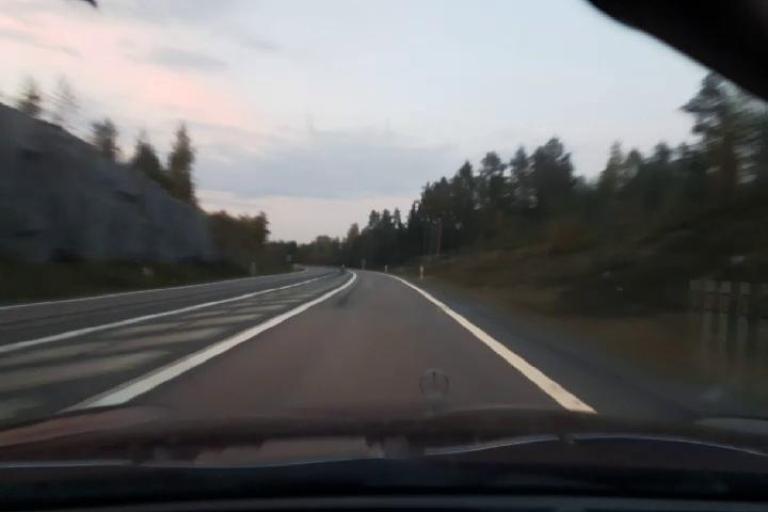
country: SE
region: Vaesternorrland
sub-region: Kramfors Kommun
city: Nordingra
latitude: 62.8851
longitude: 18.0862
